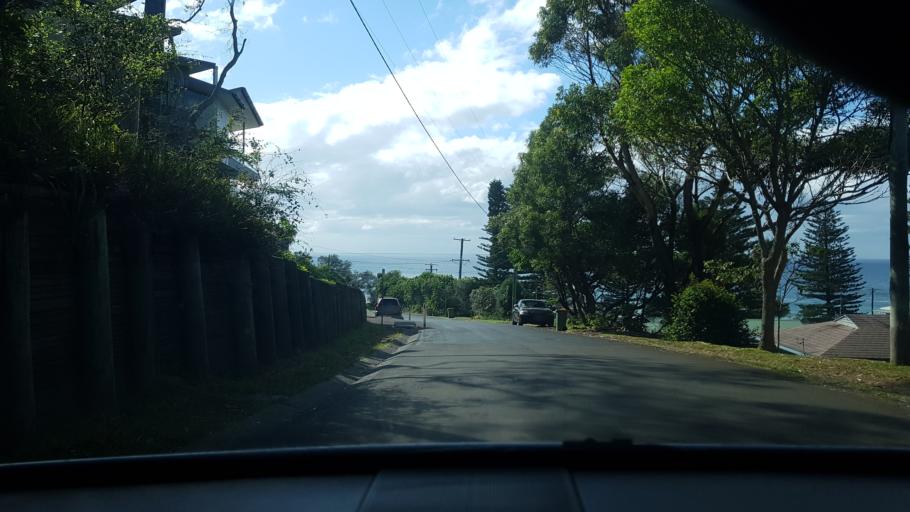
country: AU
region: New South Wales
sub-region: Gosford Shire
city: Macmasters Beach
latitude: -33.4991
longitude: 151.4227
